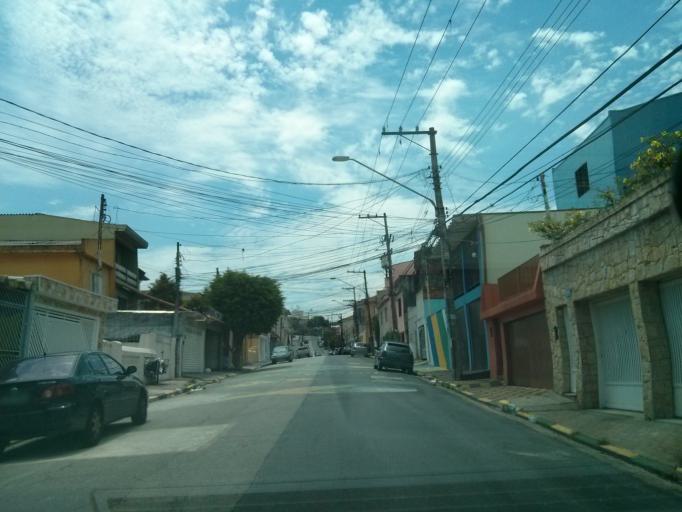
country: BR
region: Sao Paulo
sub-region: Sao Caetano Do Sul
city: Sao Caetano do Sul
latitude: -23.6113
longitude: -46.6137
